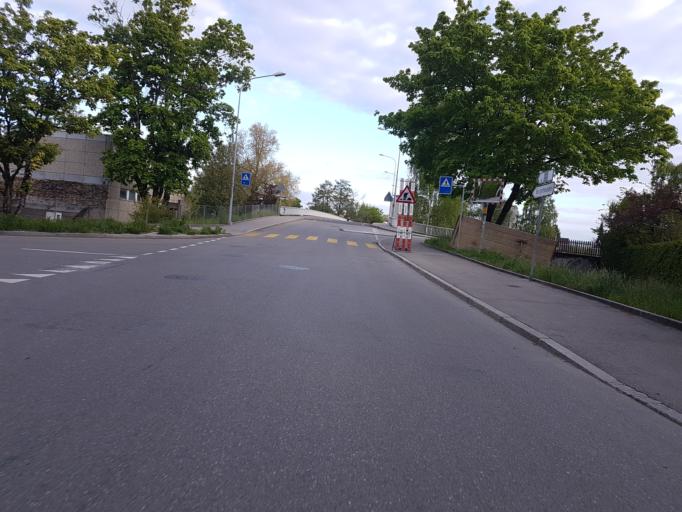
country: CH
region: Bern
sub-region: Biel/Bienne District
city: Nidau
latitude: 47.1235
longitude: 7.2371
